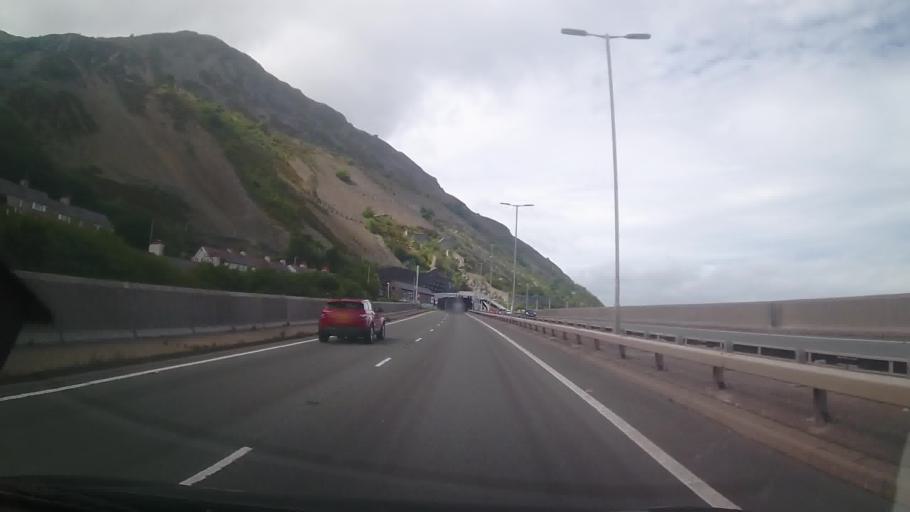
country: GB
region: Wales
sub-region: Conwy
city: Llanfairfechan
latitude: 53.2673
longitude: -3.9398
